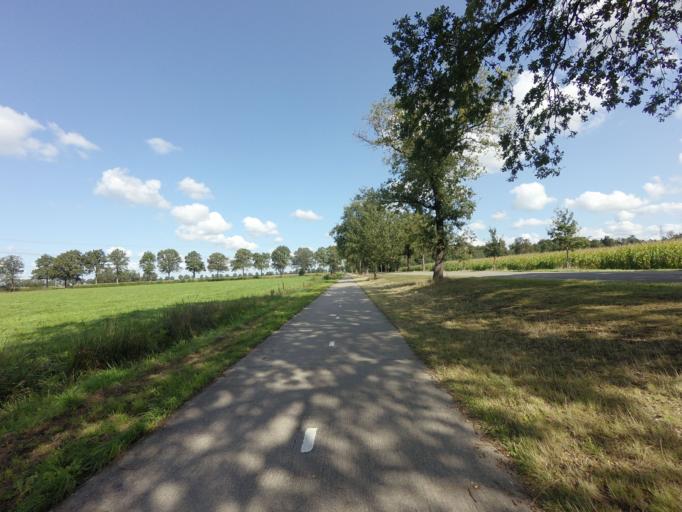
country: NL
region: Overijssel
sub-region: Gemeente Dalfsen
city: Dalfsen
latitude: 52.5404
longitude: 6.2615
